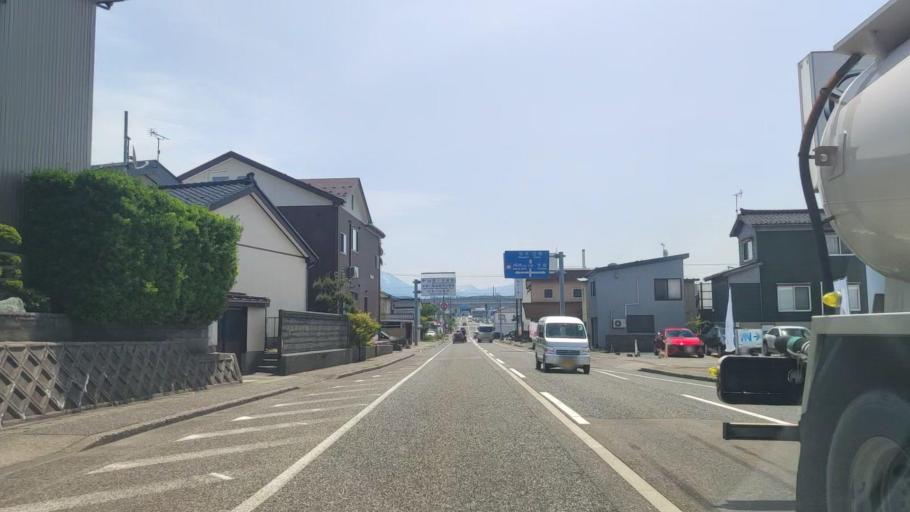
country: JP
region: Niigata
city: Itoigawa
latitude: 37.0445
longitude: 137.8505
